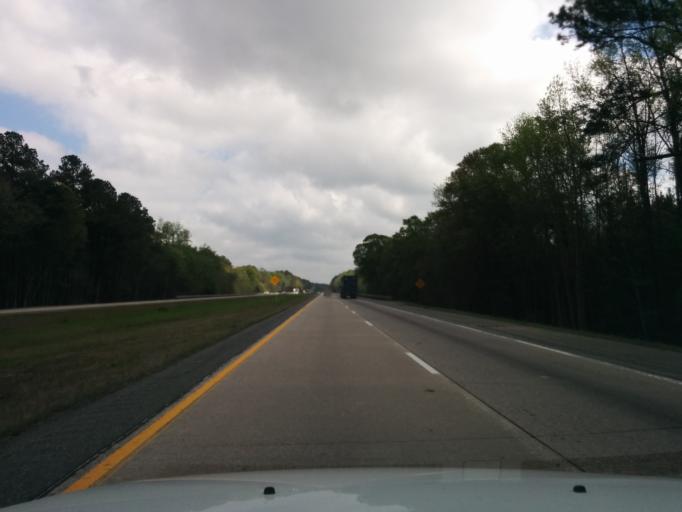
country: US
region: Georgia
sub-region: Bryan County
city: Pembroke
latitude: 32.2154
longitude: -81.5215
